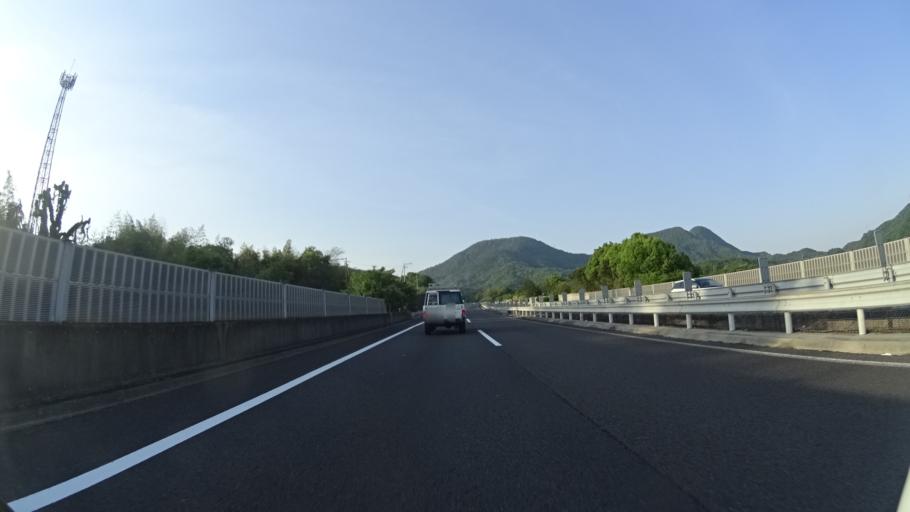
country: JP
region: Kagawa
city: Tadotsu
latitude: 34.1955
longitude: 133.7320
